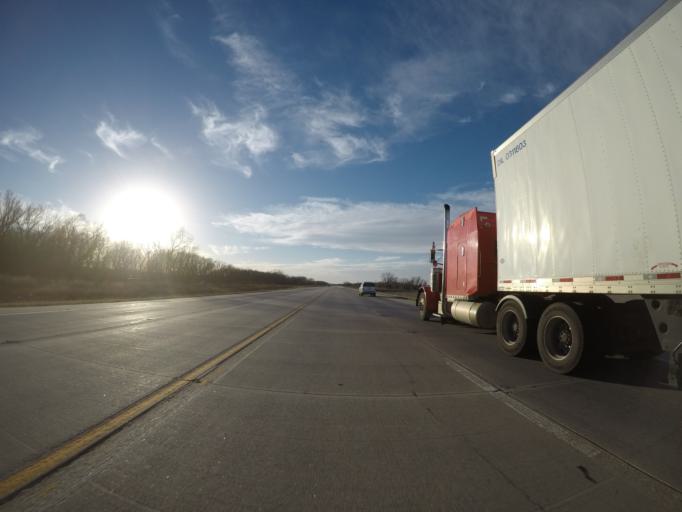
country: US
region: Kansas
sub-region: Lyon County
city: Emporia
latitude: 38.4068
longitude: -96.3526
